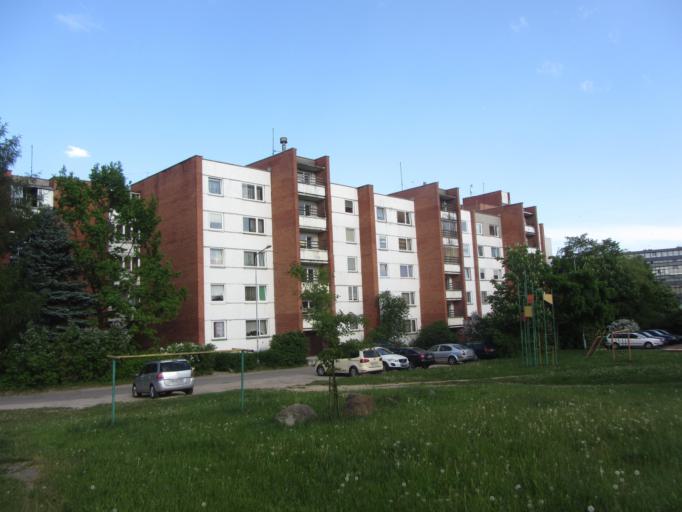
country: LT
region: Vilnius County
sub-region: Vilnius
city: Fabijoniskes
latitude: 54.7389
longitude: 25.2668
